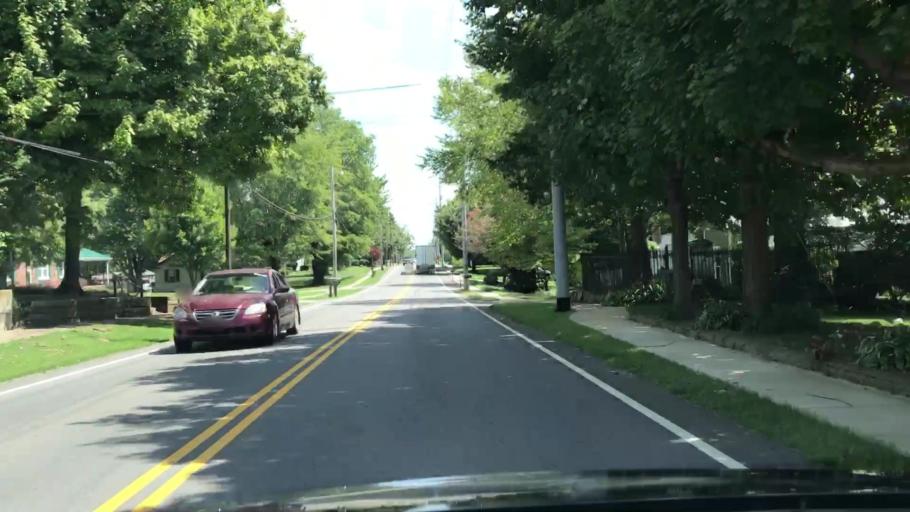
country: US
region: Tennessee
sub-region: Robertson County
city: Cross Plains
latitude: 36.5490
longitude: -86.7019
